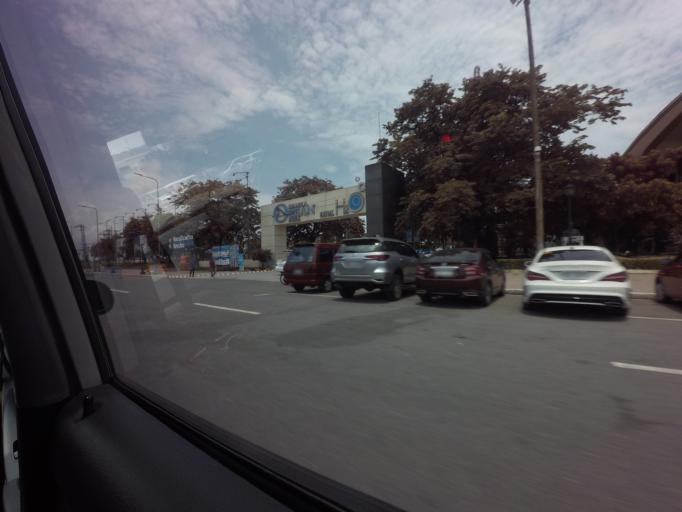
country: PH
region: Metro Manila
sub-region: City of Manila
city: Port Area
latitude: 14.5796
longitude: 120.9746
